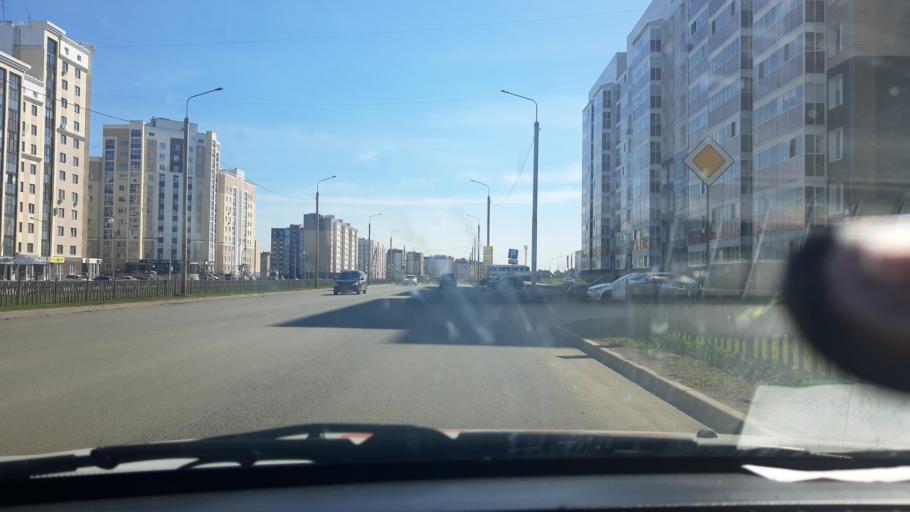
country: RU
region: Bashkortostan
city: Sterlitamak
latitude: 53.6278
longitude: 55.8957
